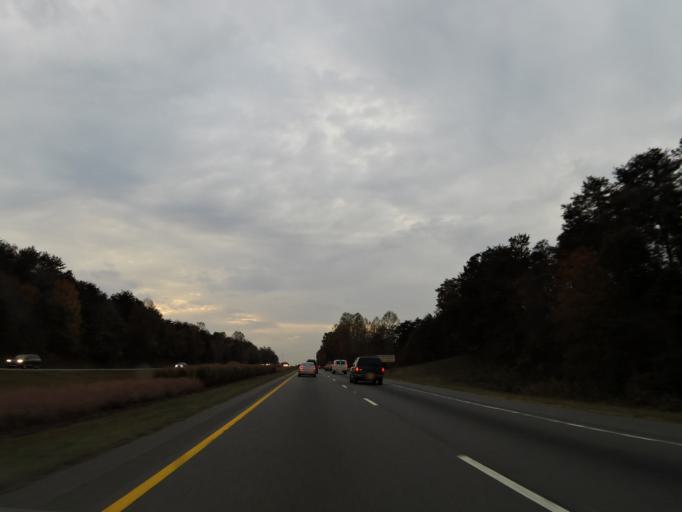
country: US
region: North Carolina
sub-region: Burke County
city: Hildebran
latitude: 35.7057
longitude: -81.4103
